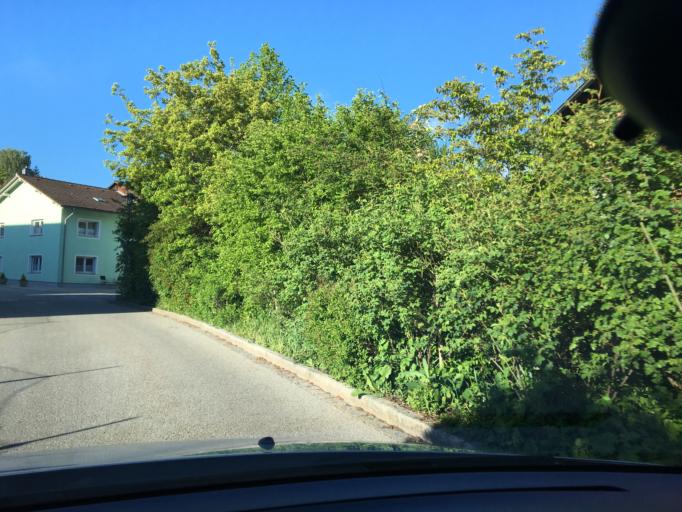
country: DE
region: Bavaria
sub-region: Lower Bavaria
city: Schalkham
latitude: 48.4964
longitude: 12.3749
